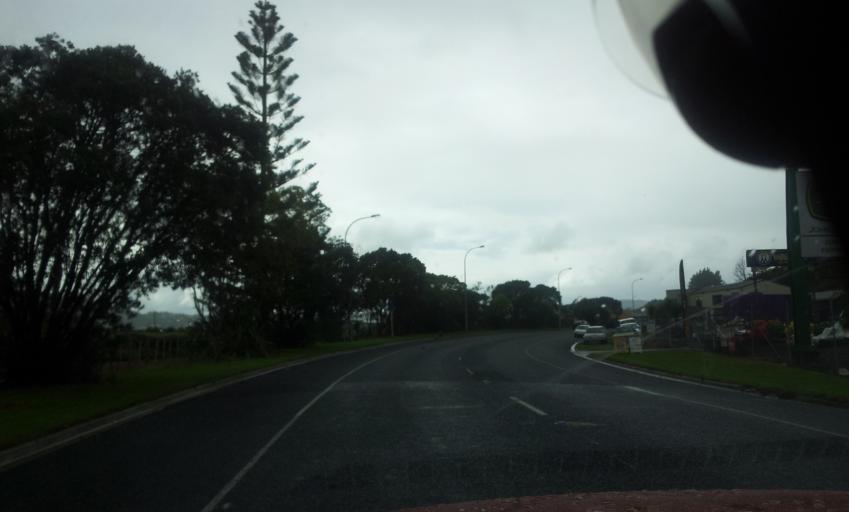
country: NZ
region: Northland
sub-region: Whangarei
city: Whangarei
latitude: -35.7447
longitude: 174.3247
